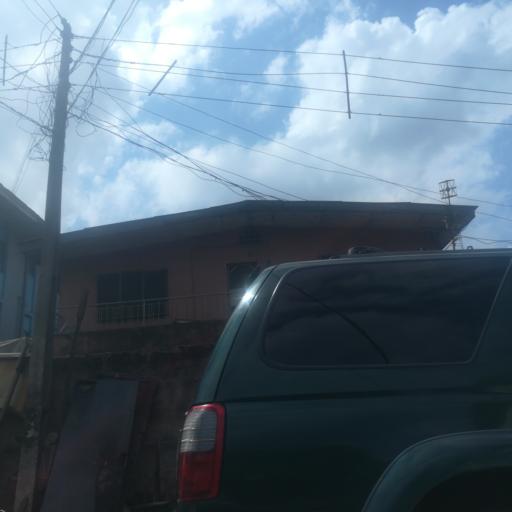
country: NG
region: Lagos
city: Ojota
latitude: 6.6002
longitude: 3.3896
